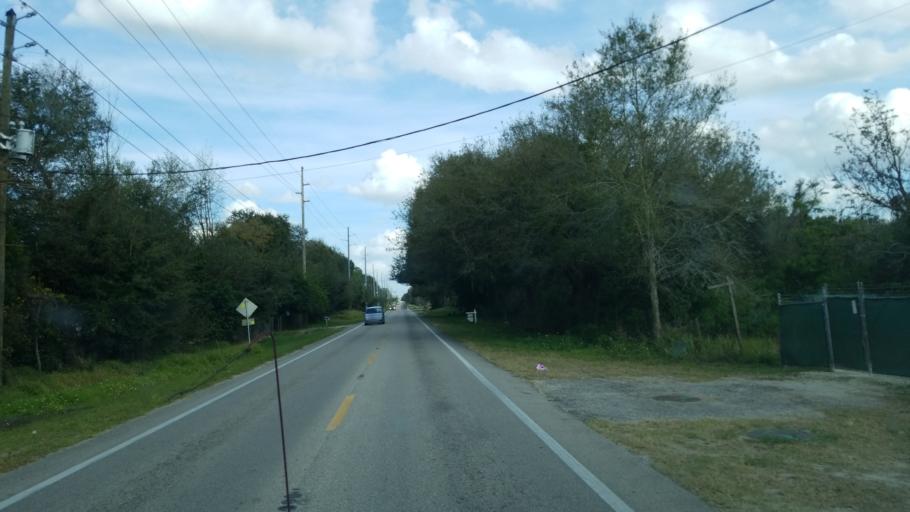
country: US
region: Florida
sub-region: Polk County
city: Haines City
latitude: 28.1141
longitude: -81.6059
